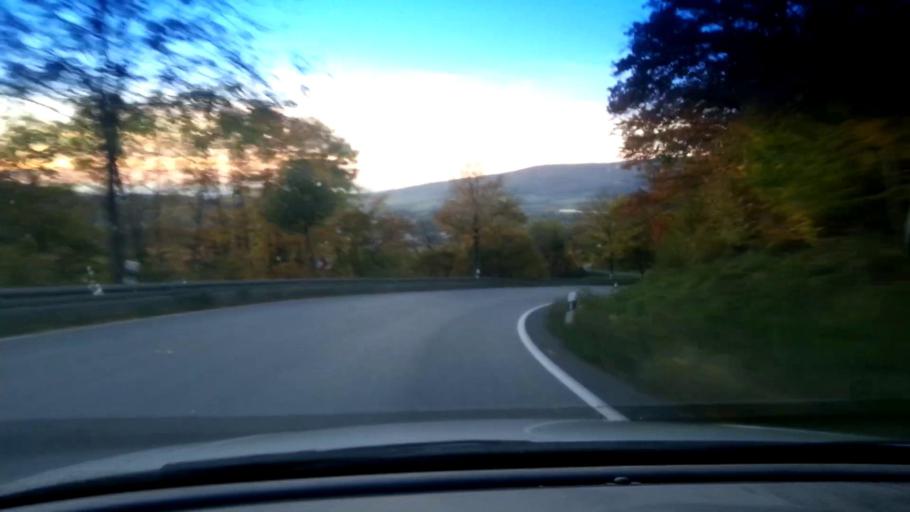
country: DE
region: Bavaria
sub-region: Upper Franconia
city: Litzendorf
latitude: 49.8698
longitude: 11.0756
